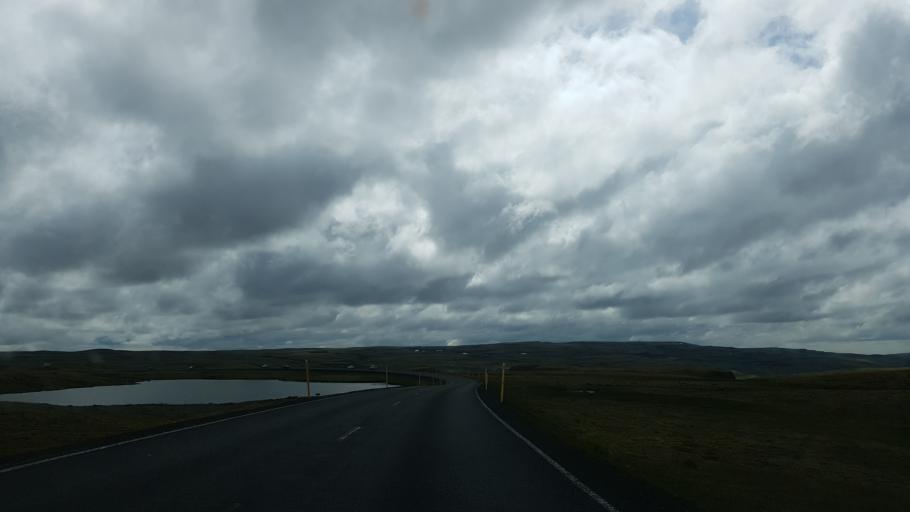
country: IS
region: West
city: Borgarnes
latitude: 64.9494
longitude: -21.0557
